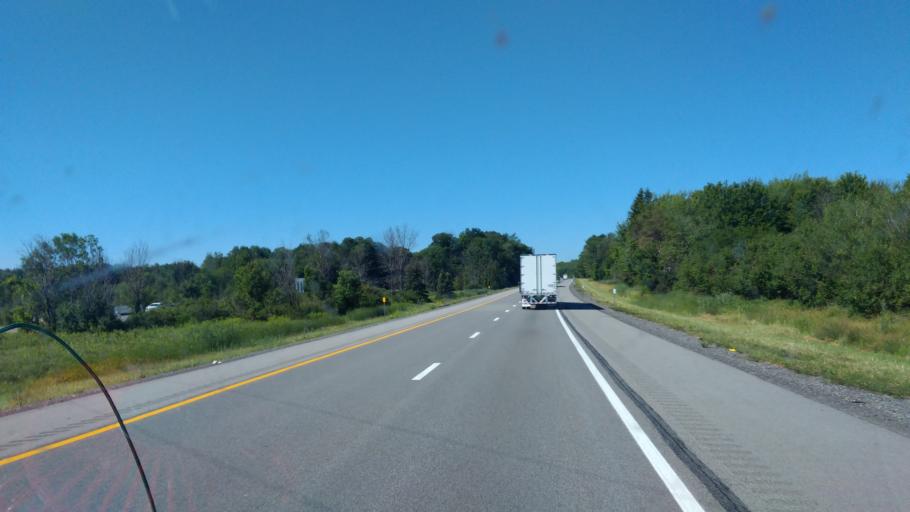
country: US
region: New York
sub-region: Erie County
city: Angola
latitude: 42.6490
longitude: -78.9724
